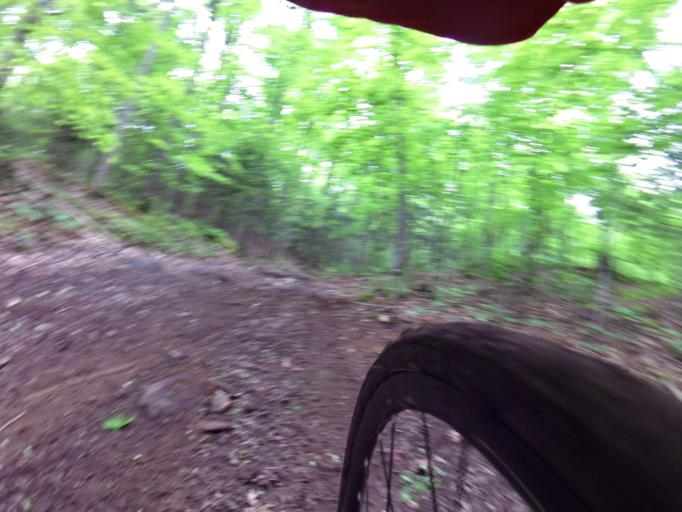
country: CA
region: Ontario
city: Arnprior
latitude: 45.1895
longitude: -76.5346
